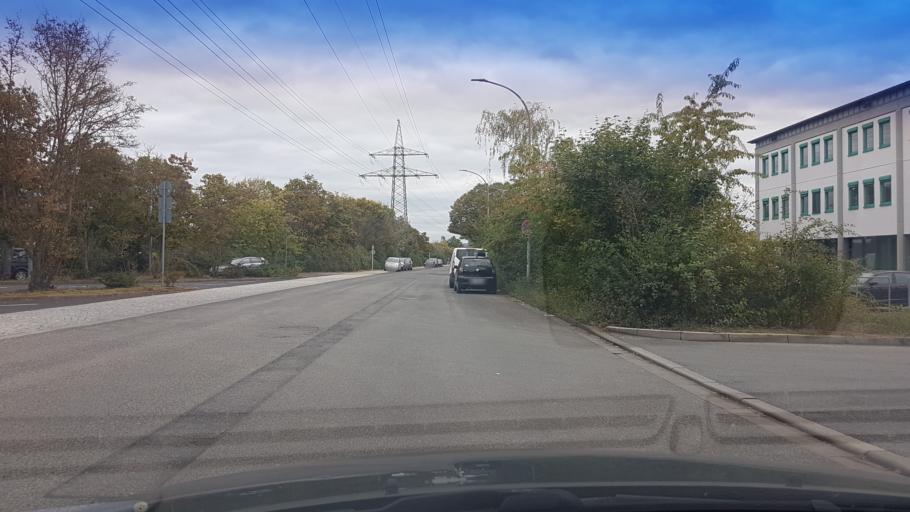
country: DE
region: Bavaria
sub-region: Upper Franconia
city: Bamberg
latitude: 49.9181
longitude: 10.8946
